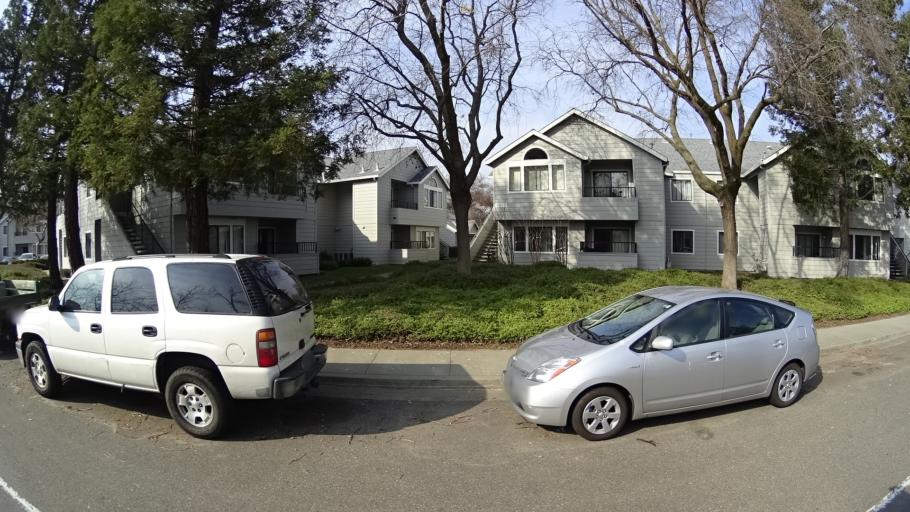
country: US
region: California
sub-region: Yolo County
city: Davis
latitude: 38.5548
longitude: -121.7807
